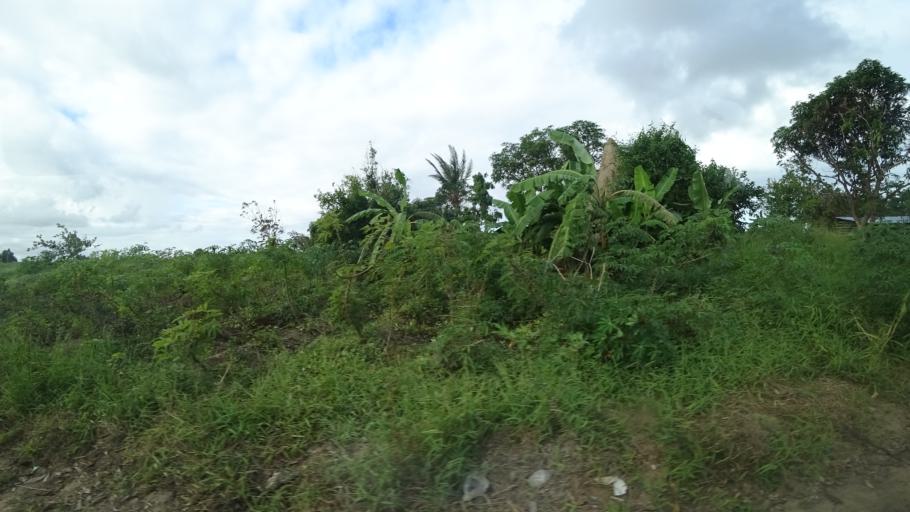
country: MZ
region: Sofala
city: Beira
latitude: -19.6572
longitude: 35.0615
